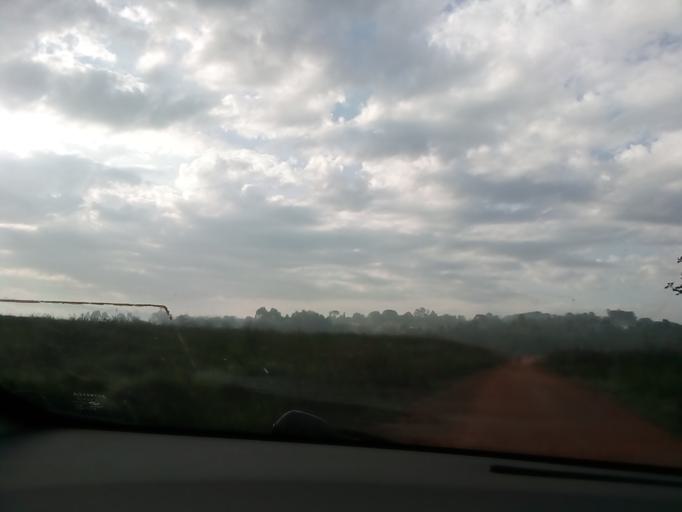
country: UG
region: Central Region
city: Masaka
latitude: -0.3450
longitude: 31.7078
